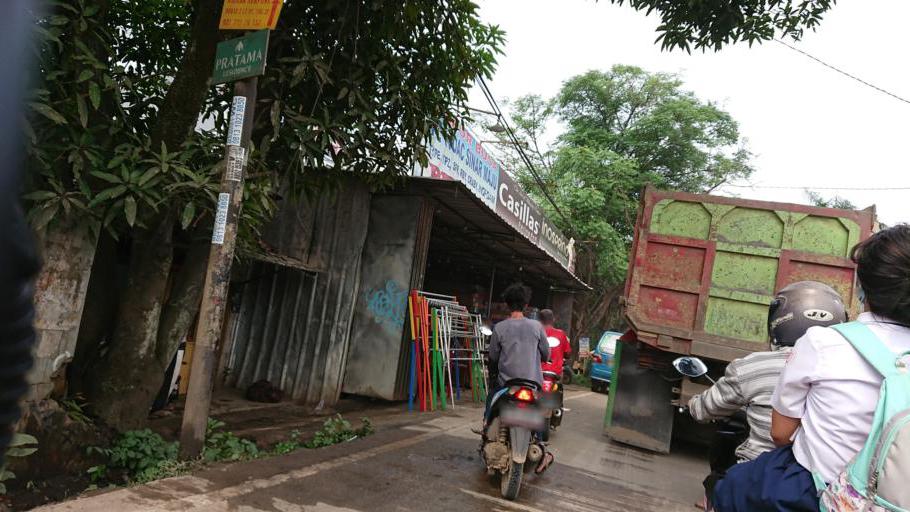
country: ID
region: West Java
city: Parung
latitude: -6.3843
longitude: 106.6816
